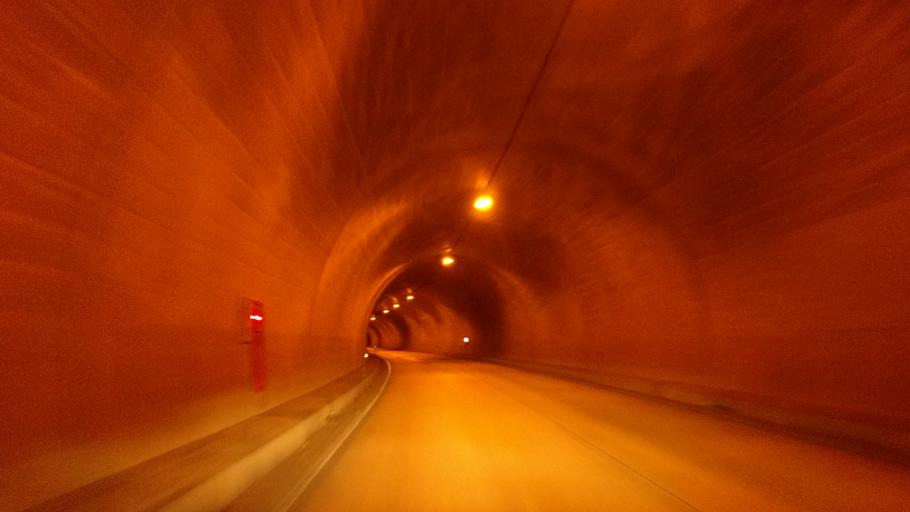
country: JP
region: Fukushima
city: Kitakata
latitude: 37.3564
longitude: 139.7752
